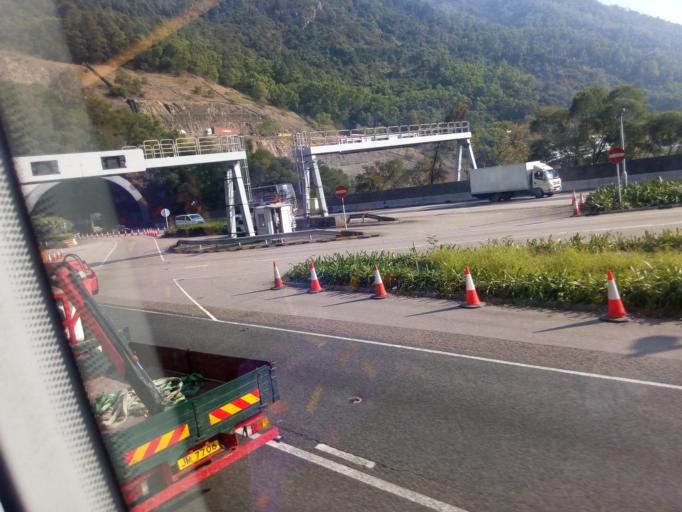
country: HK
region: Tsuen Wan
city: Tsuen Wan
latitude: 22.3449
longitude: 114.0947
